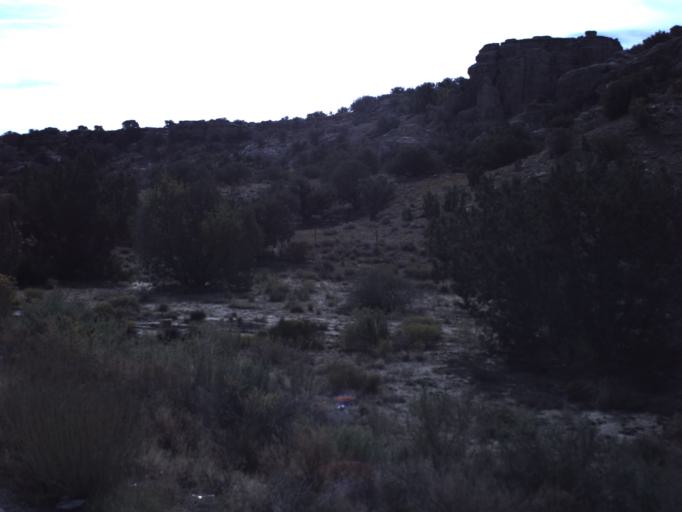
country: US
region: Utah
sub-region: San Juan County
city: Blanding
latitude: 37.4340
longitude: -109.3982
